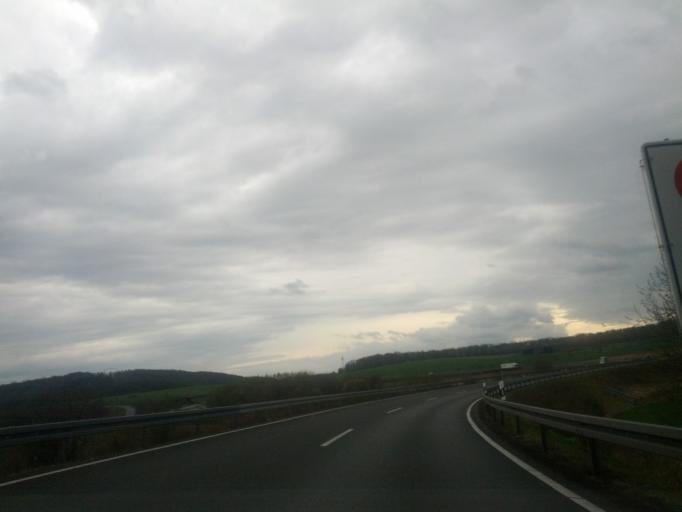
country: DE
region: Lower Saxony
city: Rosdorf
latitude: 51.4588
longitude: 9.8680
